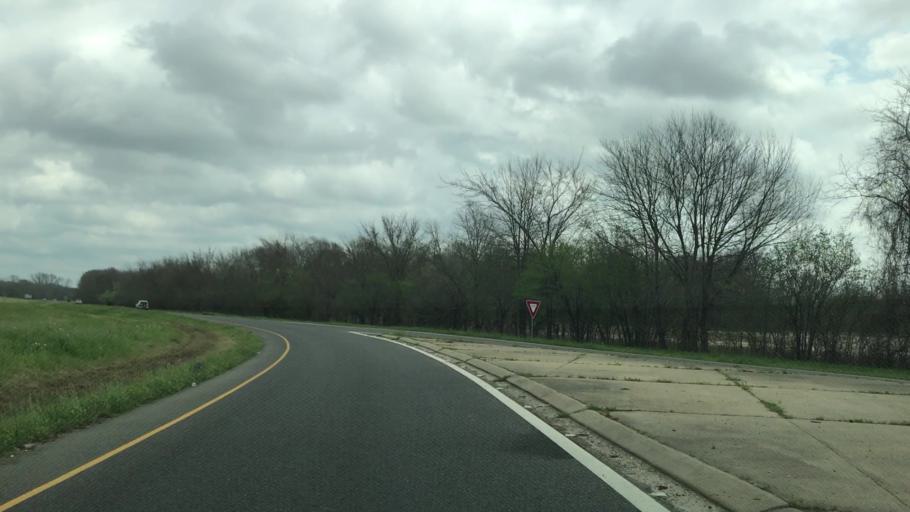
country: US
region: Louisiana
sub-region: Rapides Parish
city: Boyce
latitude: 31.3786
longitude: -92.6694
